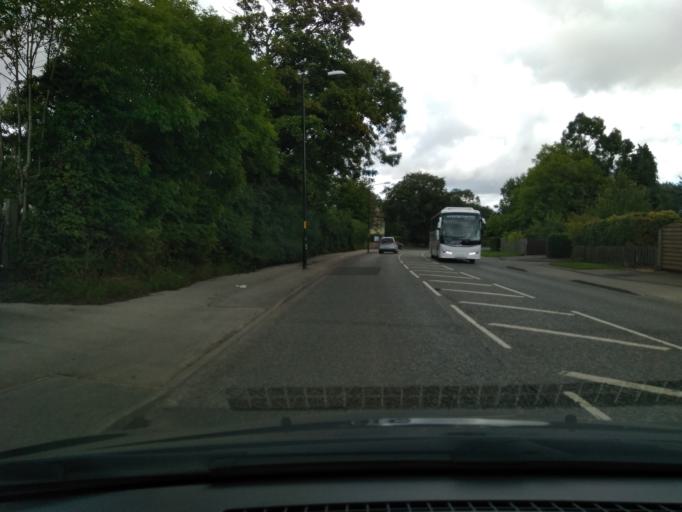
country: GB
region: England
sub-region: North Yorkshire
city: Knaresborough
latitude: 54.0037
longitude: -1.4933
